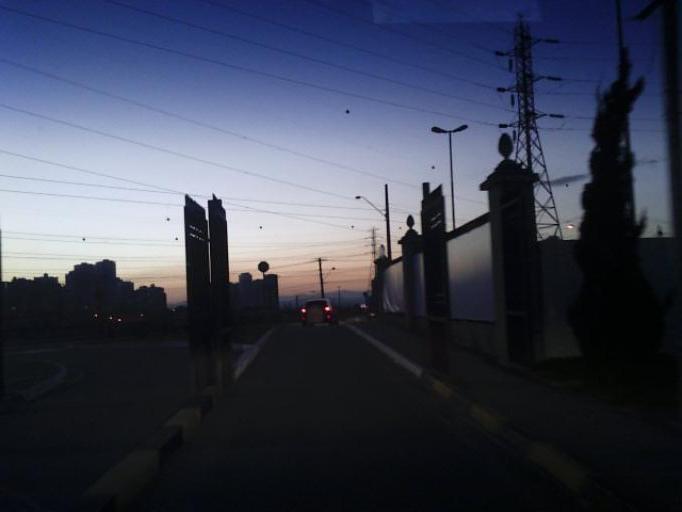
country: BR
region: Sao Paulo
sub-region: Sao Jose Dos Campos
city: Sao Jose dos Campos
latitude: -23.2185
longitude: -45.8964
